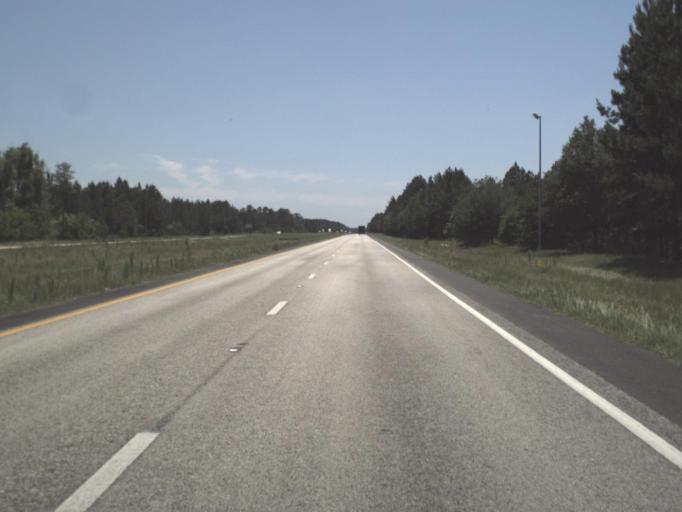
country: US
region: Florida
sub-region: Clay County
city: Bellair-Meadowbrook Terrace
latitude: 30.2136
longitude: -81.8376
